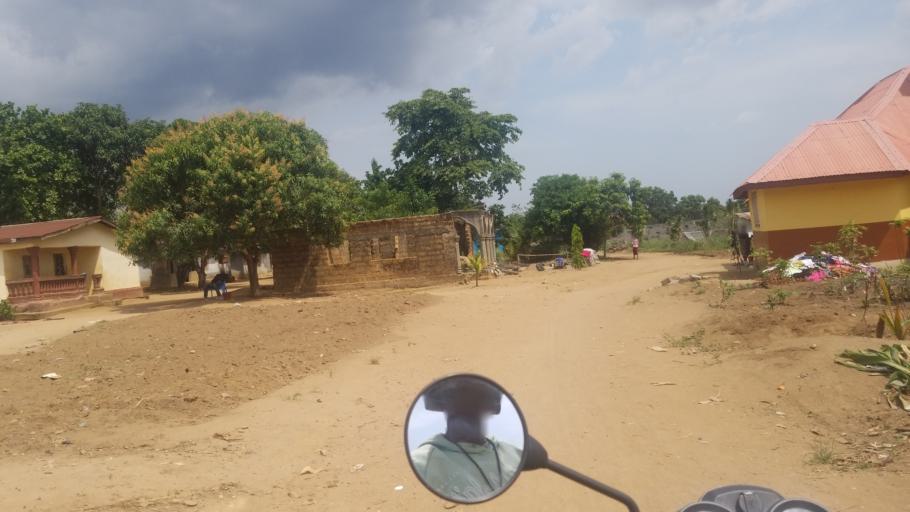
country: SL
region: Western Area
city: Waterloo
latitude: 8.3179
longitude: -13.0466
